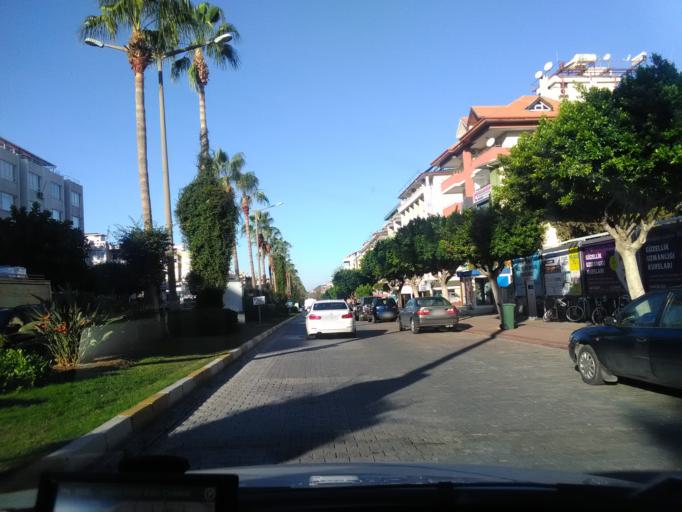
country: TR
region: Antalya
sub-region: Alanya
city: Alanya
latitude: 36.5446
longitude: 31.9953
